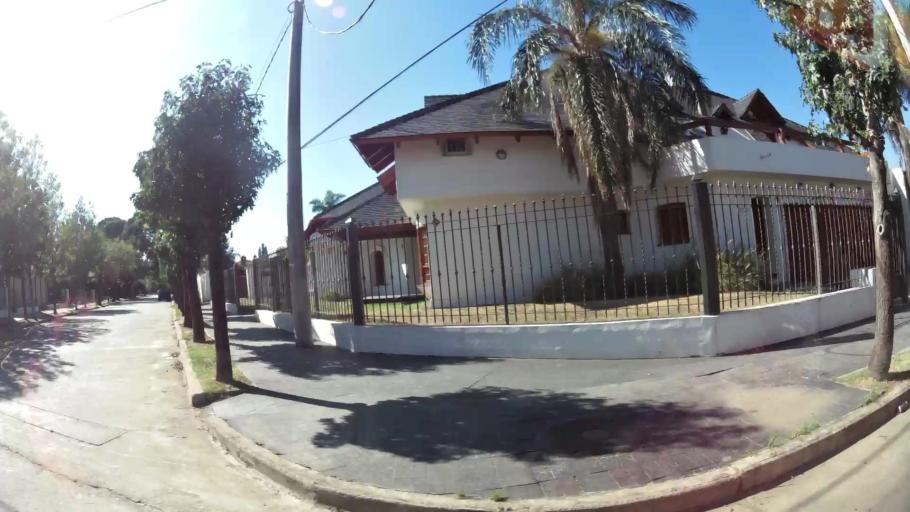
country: AR
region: Cordoba
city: Villa Allende
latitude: -31.3488
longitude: -64.2452
